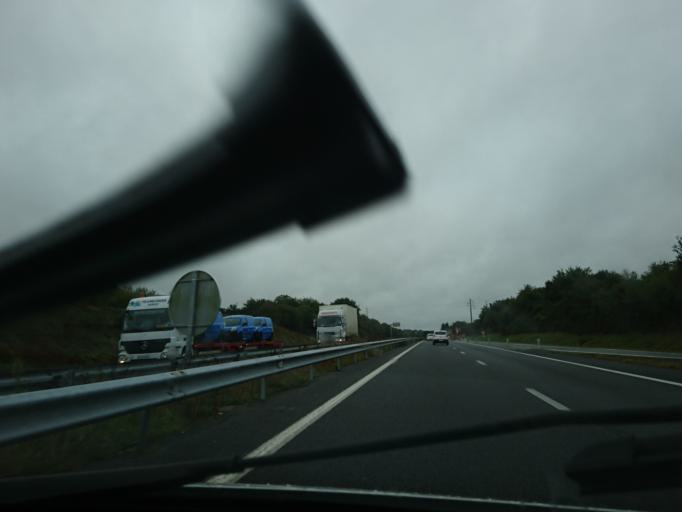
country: FR
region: Brittany
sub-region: Departement du Morbihan
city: Nivillac
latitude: 47.5200
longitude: -2.2803
